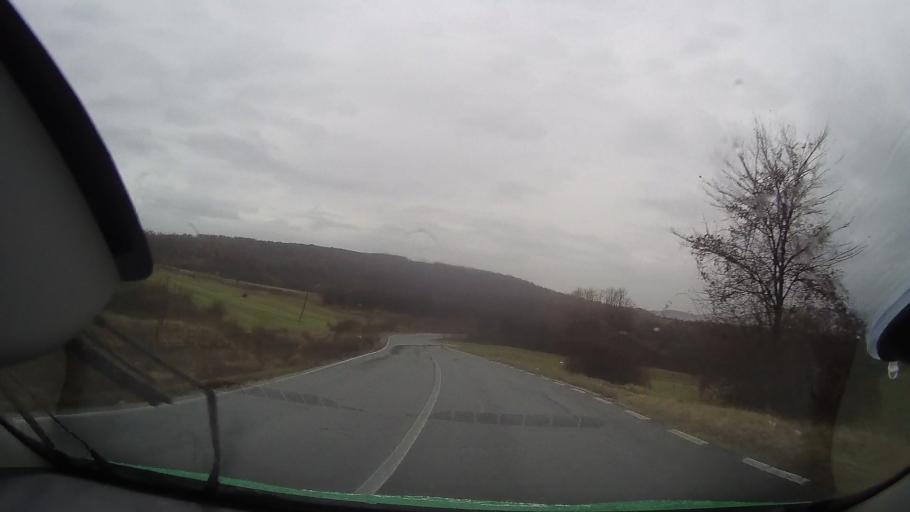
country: RO
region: Bihor
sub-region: Comuna Rabagani
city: Rabagani
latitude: 46.7299
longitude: 22.2337
